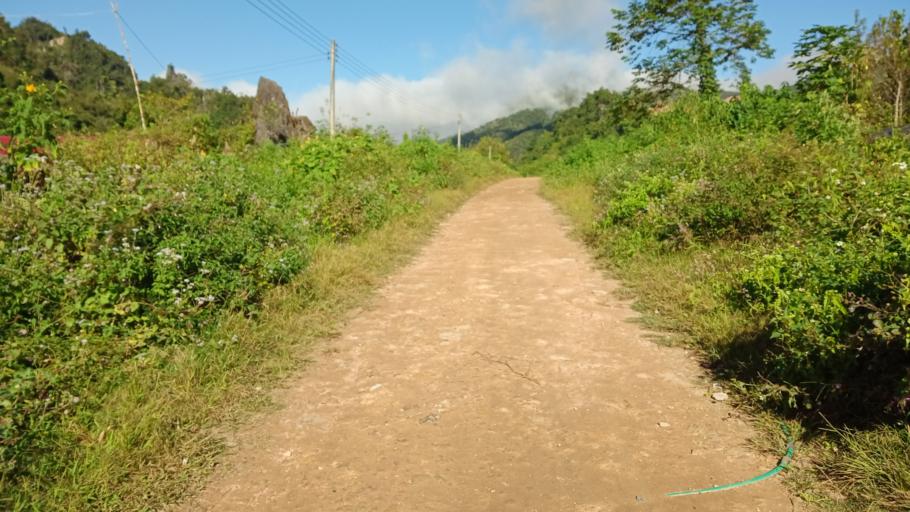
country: LA
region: Xiangkhoang
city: Phonsavan
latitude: 19.1140
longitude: 102.9134
